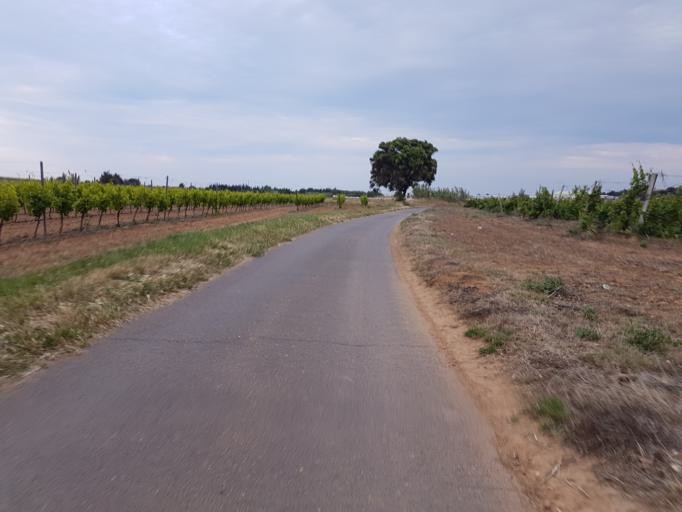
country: FR
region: Languedoc-Roussillon
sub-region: Departement de l'Herault
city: Portiragnes
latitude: 43.3163
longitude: 3.3345
